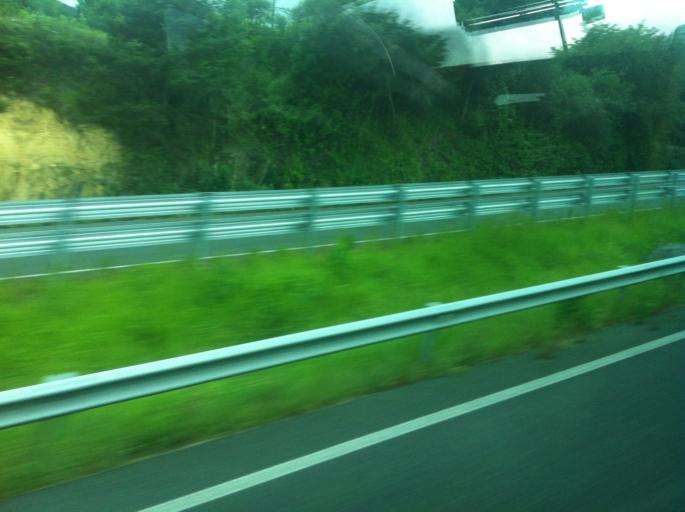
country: ES
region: Basque Country
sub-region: Bizkaia
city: Arrigorriaga
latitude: 43.2055
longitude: -2.8927
